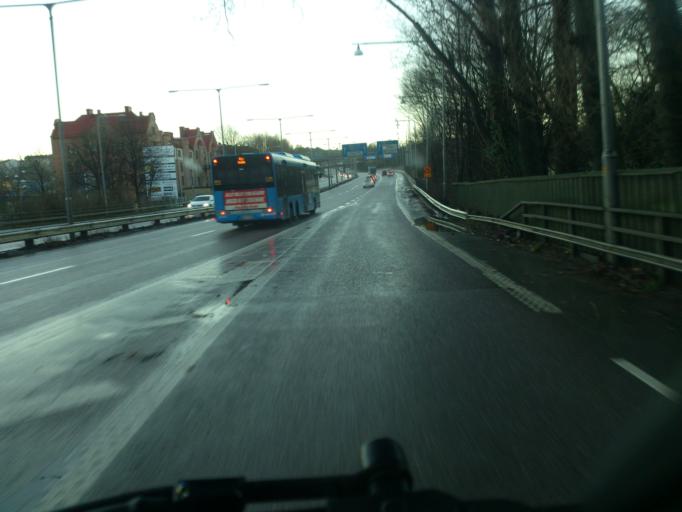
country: SE
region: Vaestra Goetaland
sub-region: Goteborg
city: Majorna
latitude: 57.6907
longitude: 11.9119
